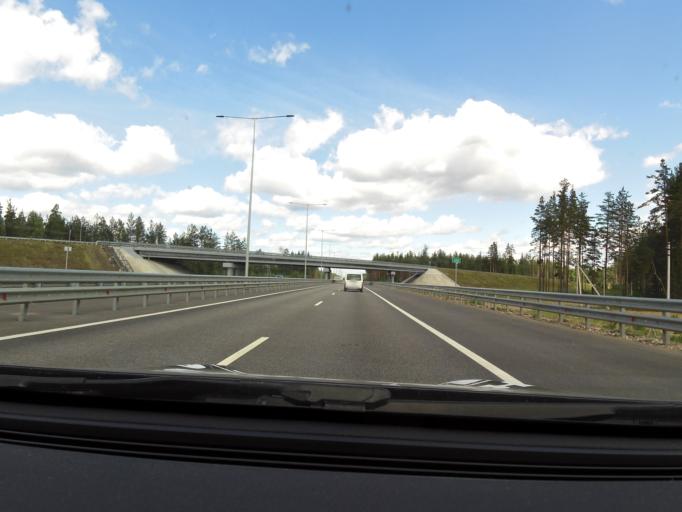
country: RU
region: Tverskaya
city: Krasnomayskiy
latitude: 57.5556
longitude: 34.2677
